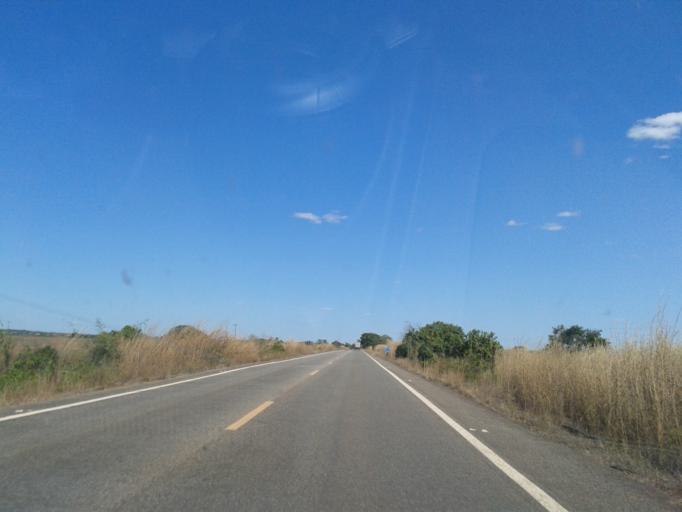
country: BR
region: Goias
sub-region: Sao Miguel Do Araguaia
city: Sao Miguel do Araguaia
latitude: -13.6003
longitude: -50.3193
